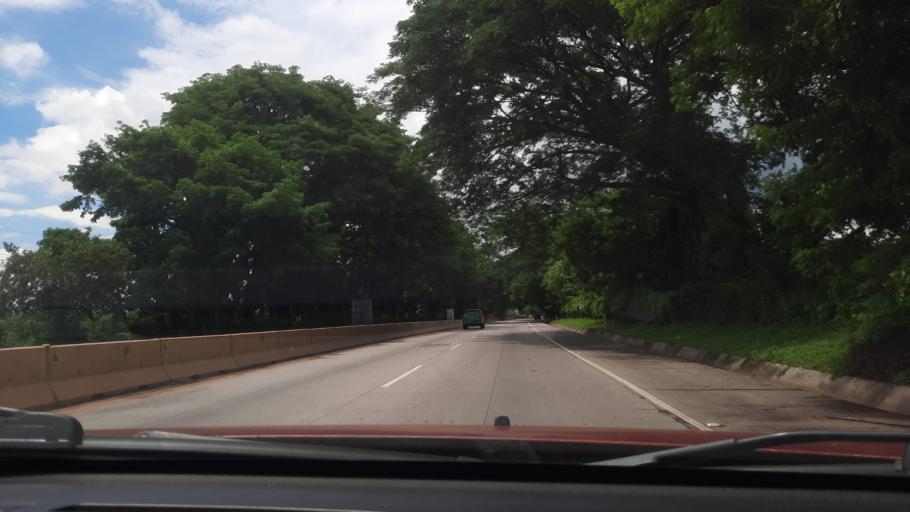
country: SV
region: Sonsonate
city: Sonsonate
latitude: 13.7151
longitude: -89.7095
